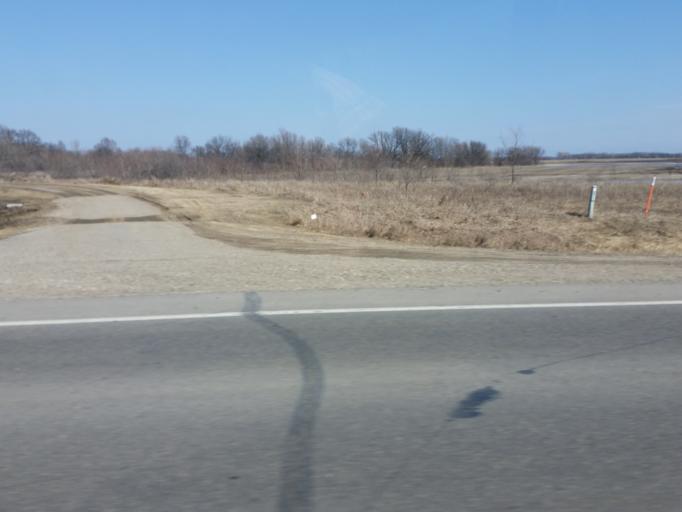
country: US
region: North Dakota
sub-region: Grand Forks County
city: Grand Forks
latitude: 48.0820
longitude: -97.1802
